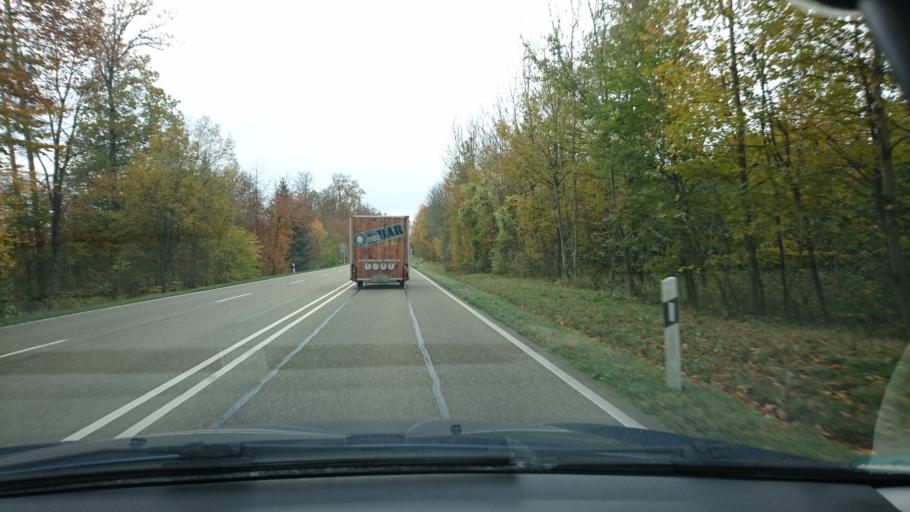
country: DE
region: Baden-Wuerttemberg
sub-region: Regierungsbezirk Stuttgart
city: Urbach
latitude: 48.8514
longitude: 9.5635
